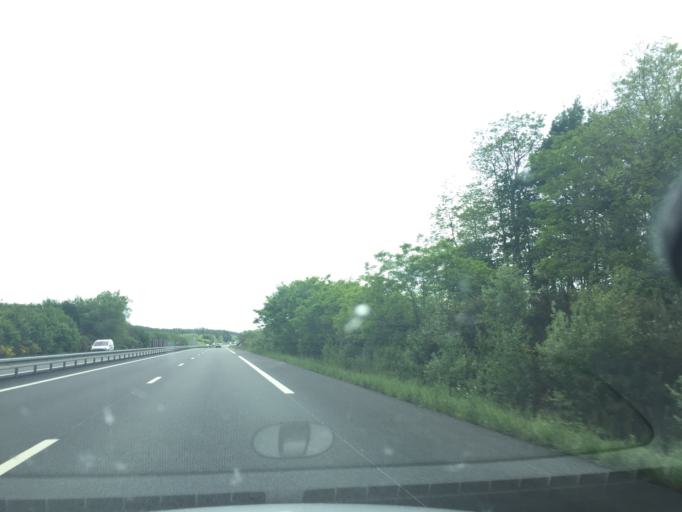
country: FR
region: Pays de la Loire
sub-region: Departement de la Sarthe
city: Brette-les-Pins
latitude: 47.9388
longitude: 0.3140
